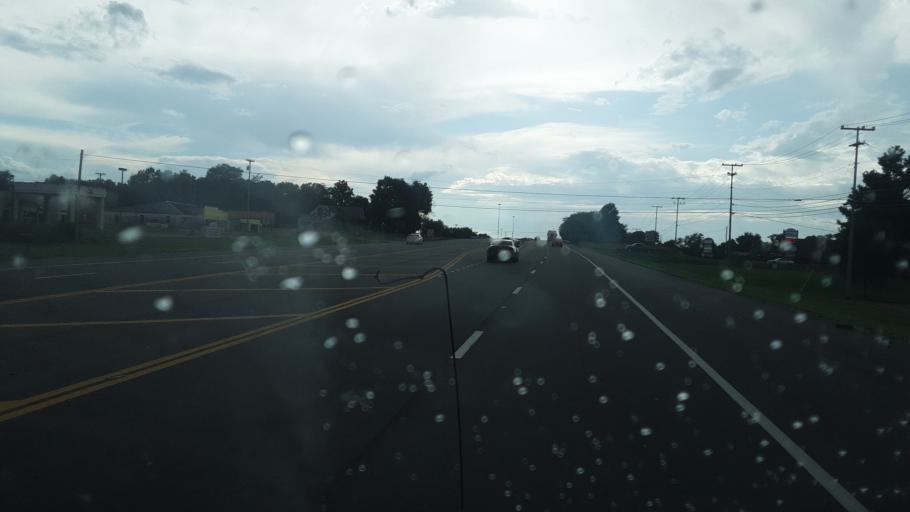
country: US
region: Tennessee
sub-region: Montgomery County
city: Clarksville
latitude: 36.5713
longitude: -87.2950
